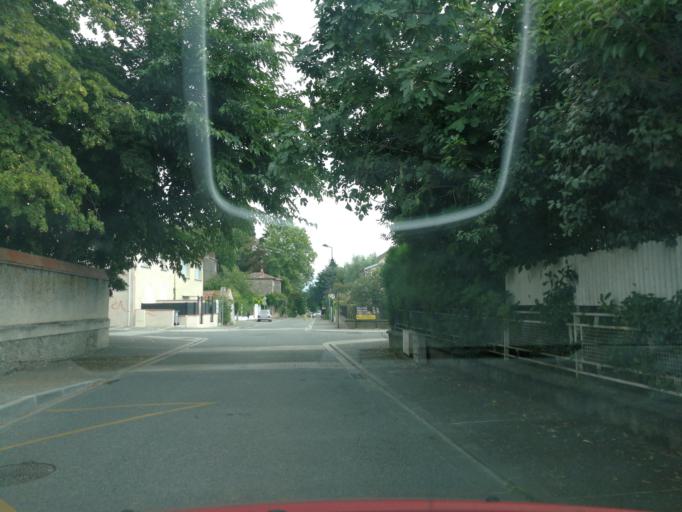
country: FR
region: Midi-Pyrenees
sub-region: Departement de la Haute-Garonne
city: Auzeville-Tolosane
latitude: 43.5300
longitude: 1.4794
